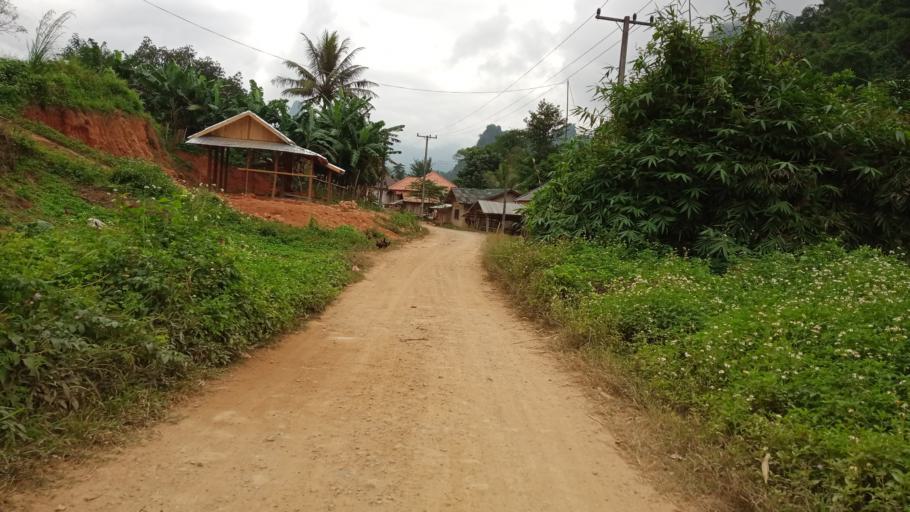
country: LA
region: Xiangkhoang
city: Phonsavan
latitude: 19.0936
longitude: 103.0002
